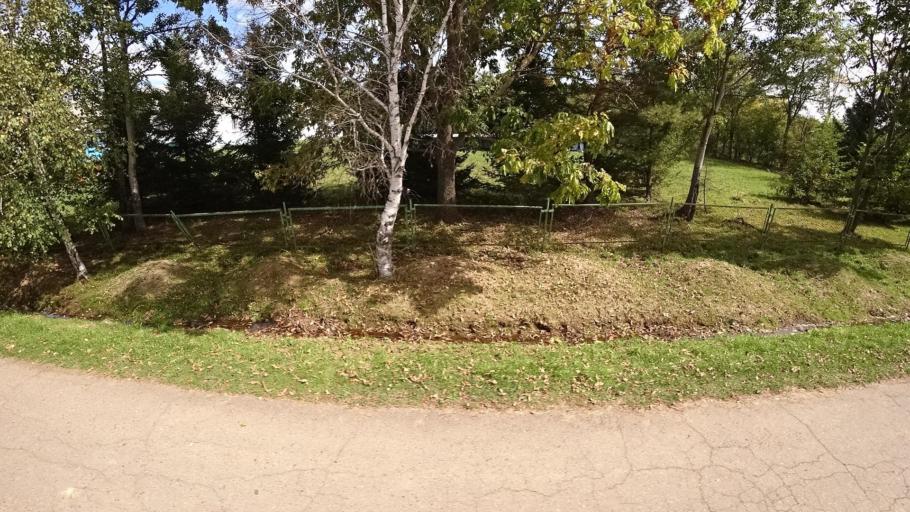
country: RU
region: Primorskiy
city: Yakovlevka
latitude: 44.6470
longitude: 133.5920
